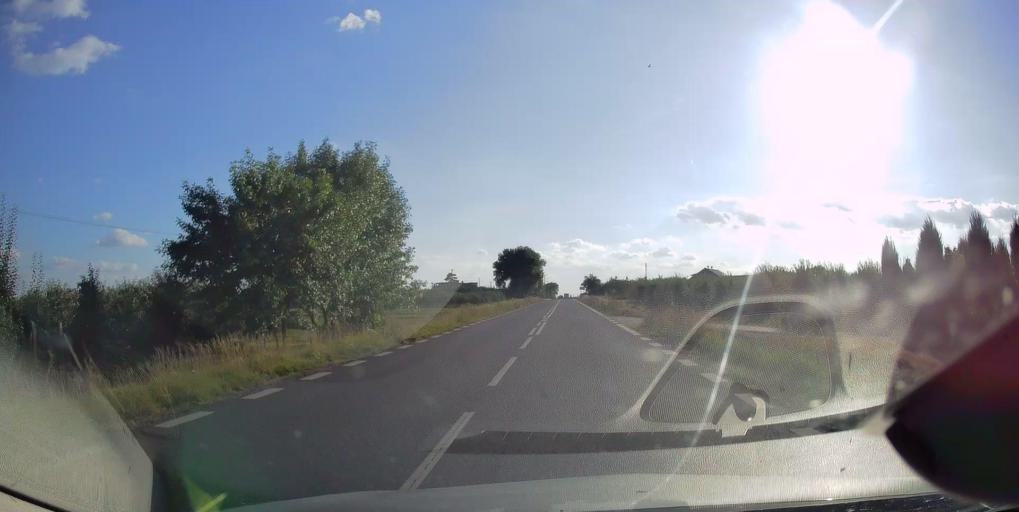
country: PL
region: Lodz Voivodeship
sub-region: Powiat rawski
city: Biala Rawska
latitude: 51.8008
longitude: 20.5390
